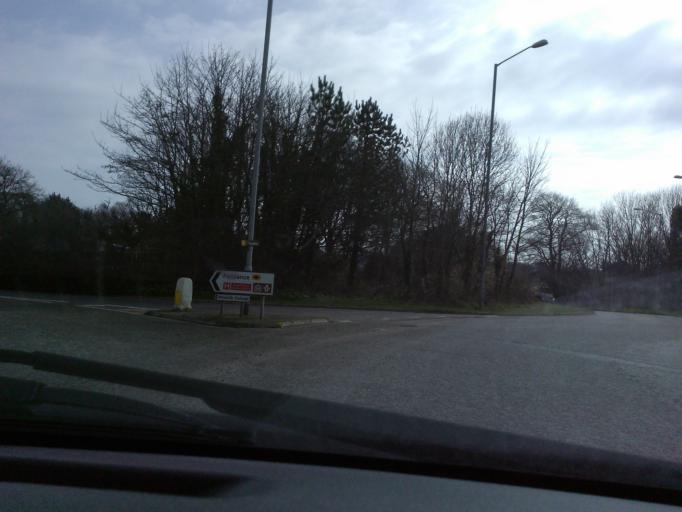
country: GB
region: England
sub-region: Cornwall
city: Penzance
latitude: 50.1255
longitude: -5.5491
